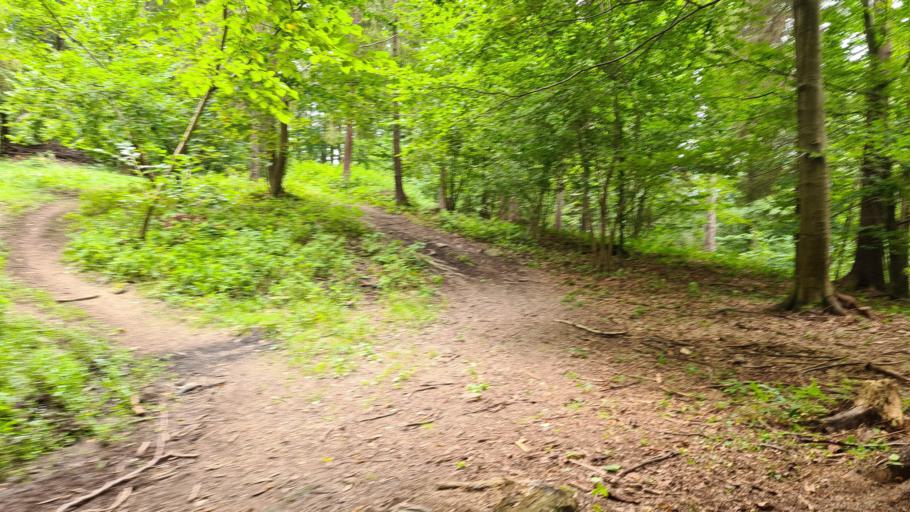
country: PL
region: Lesser Poland Voivodeship
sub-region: Powiat nowosadecki
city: Piwniczna-Zdroj
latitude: 49.4369
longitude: 20.7252
